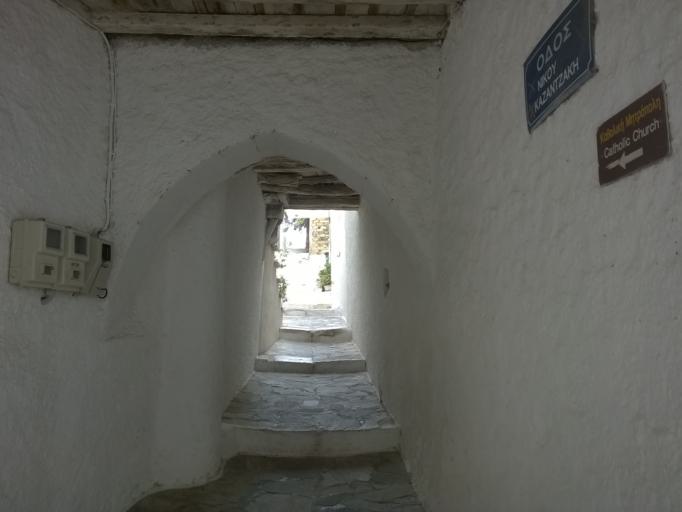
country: GR
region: South Aegean
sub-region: Nomos Kykladon
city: Naxos
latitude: 37.1054
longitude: 25.3767
